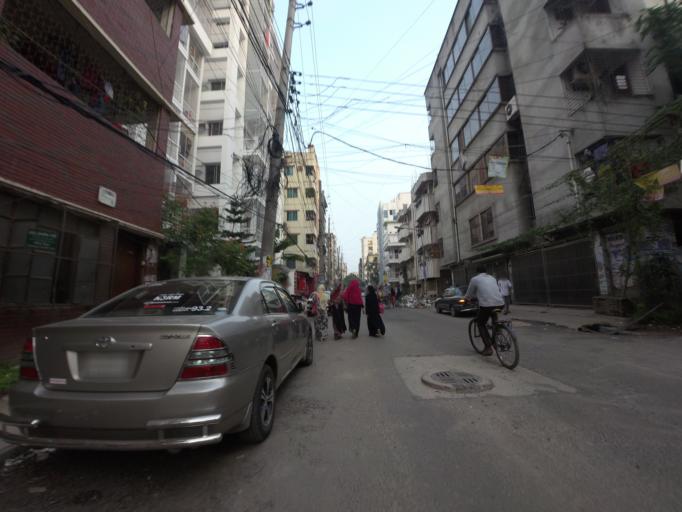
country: BD
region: Dhaka
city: Azimpur
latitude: 23.7654
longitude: 90.3644
